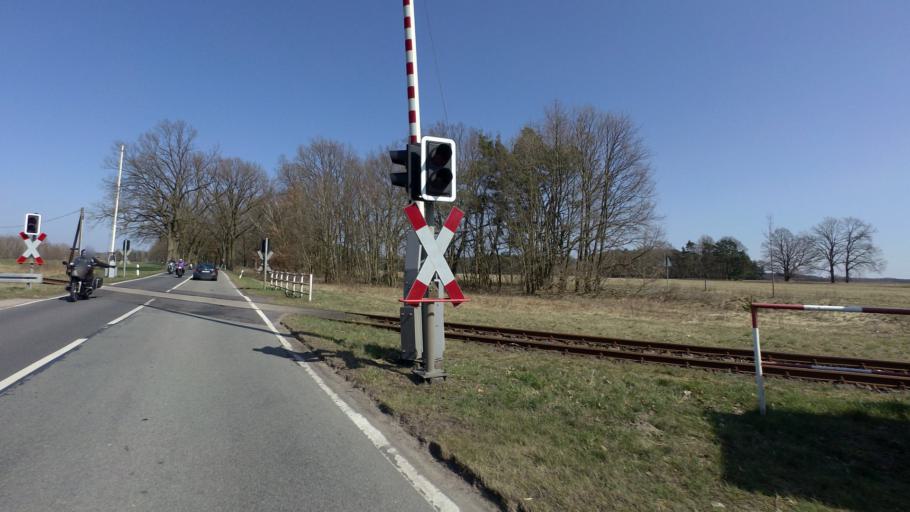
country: DE
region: Brandenburg
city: Lindow
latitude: 52.9493
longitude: 12.9785
